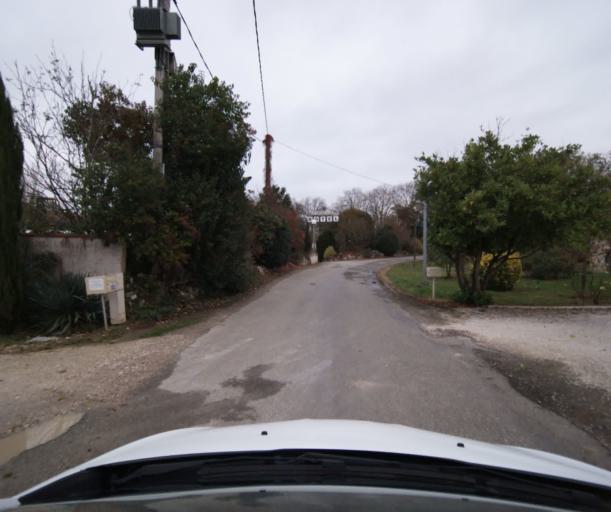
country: FR
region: Midi-Pyrenees
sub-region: Departement du Tarn-et-Garonne
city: Moissac
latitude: 44.0766
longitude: 1.0970
